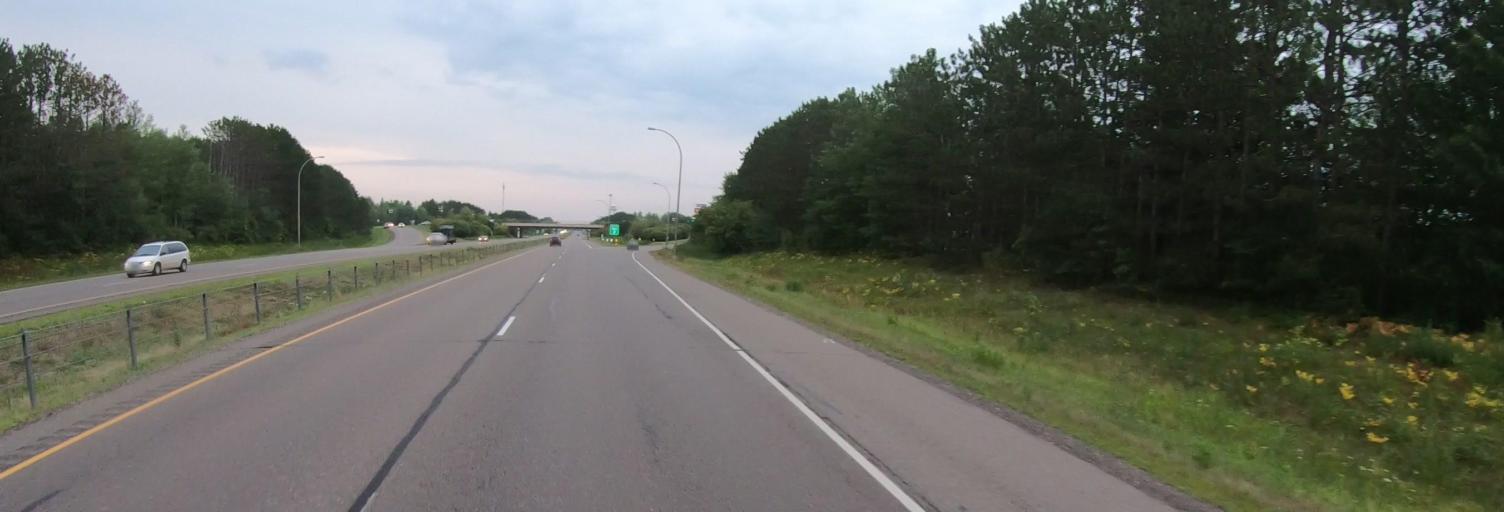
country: US
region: Minnesota
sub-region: Pine County
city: Hinckley
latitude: 46.0080
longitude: -92.9333
